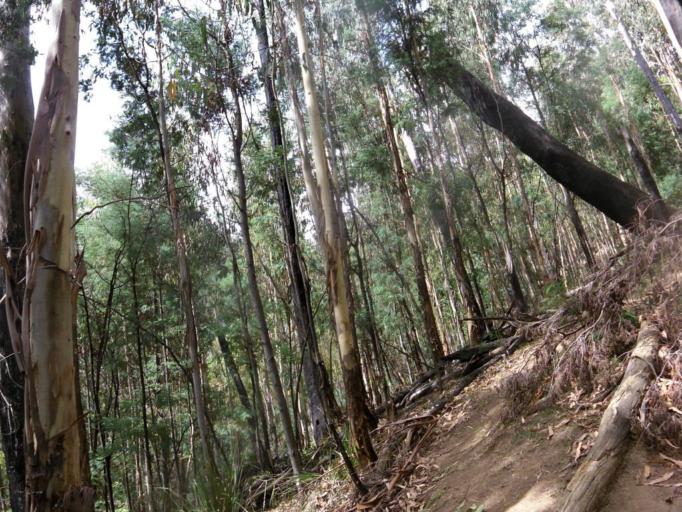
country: AU
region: Victoria
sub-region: Murrindindi
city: Alexandra
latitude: -37.4035
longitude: 145.5708
